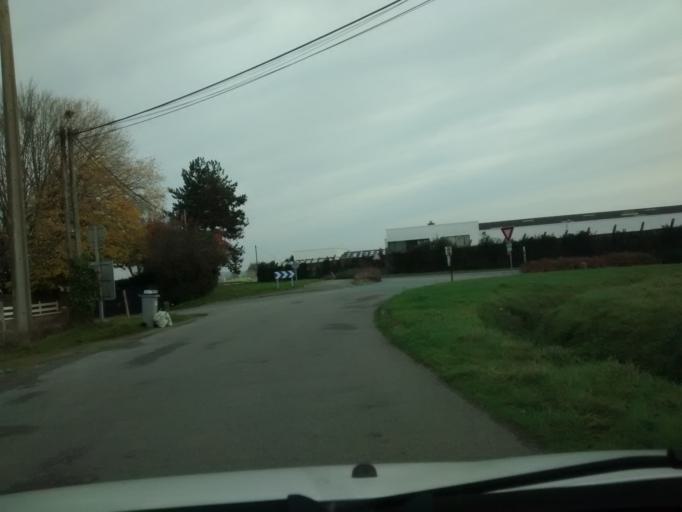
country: FR
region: Brittany
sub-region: Departement d'Ille-et-Vilaine
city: Noyal-sur-Vilaine
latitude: 48.1075
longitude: -1.5332
